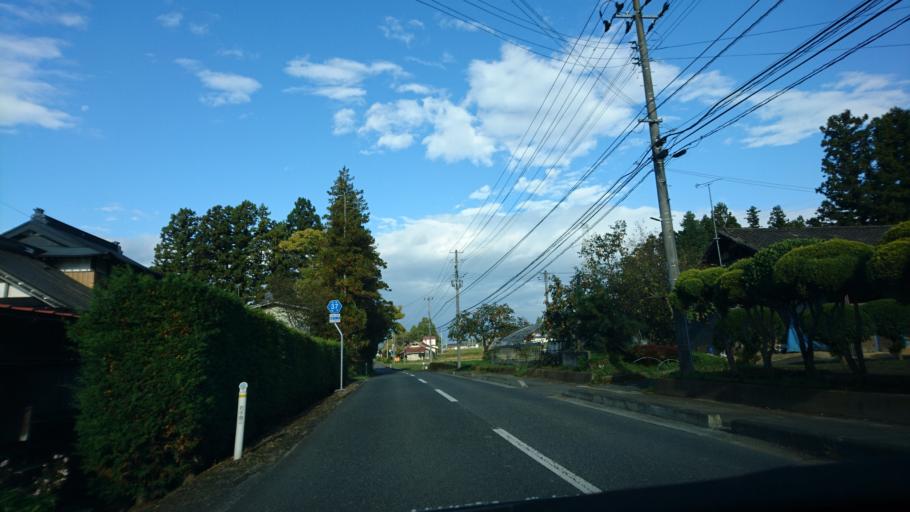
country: JP
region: Iwate
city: Ichinoseki
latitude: 39.0218
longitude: 141.0897
